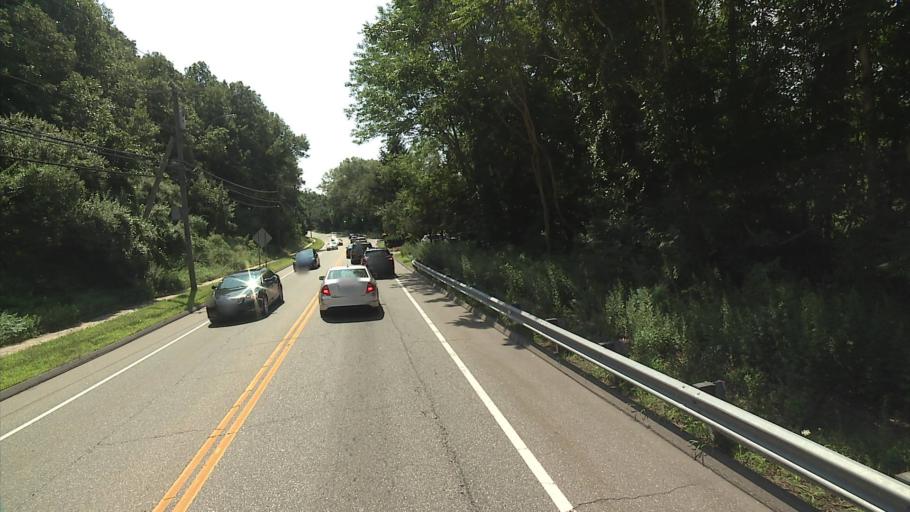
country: US
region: Connecticut
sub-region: New London County
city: Niantic
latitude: 41.3361
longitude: -72.2070
